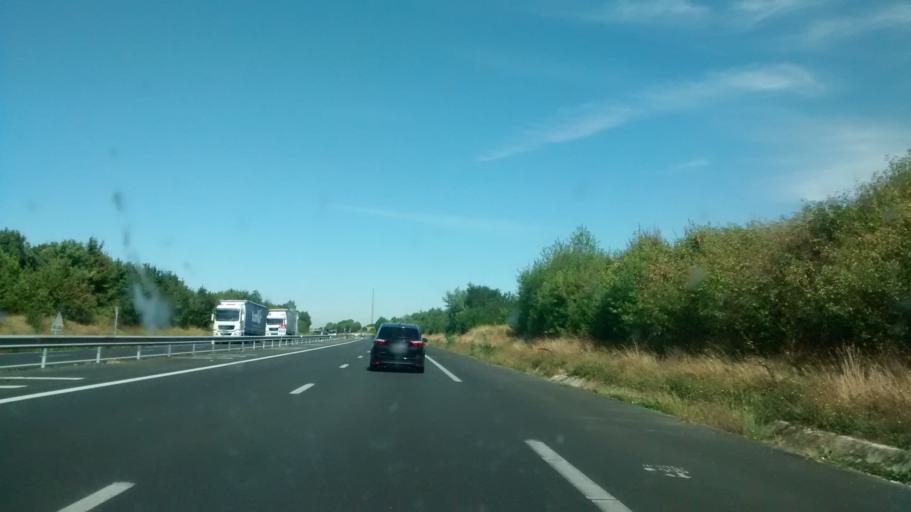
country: FR
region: Poitou-Charentes
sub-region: Departement de la Charente-Maritime
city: Saint-Jean-d'Angely
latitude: 46.0324
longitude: -0.5379
